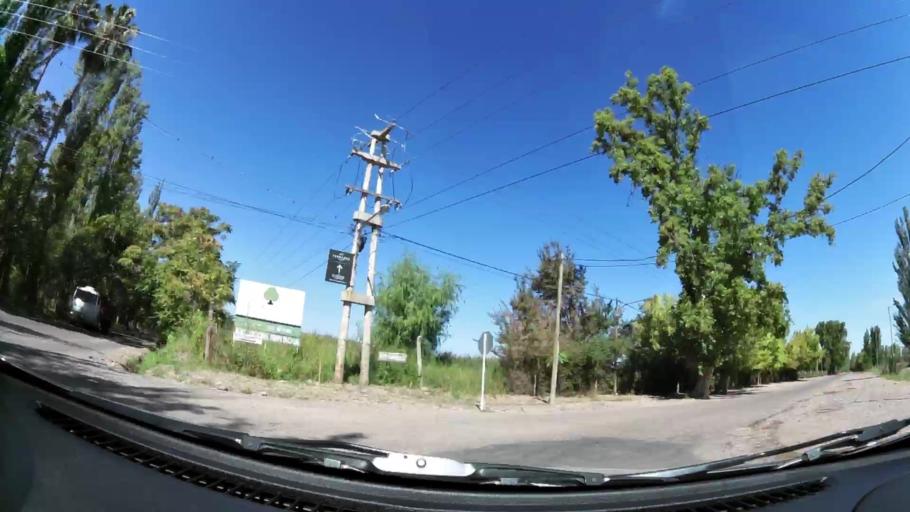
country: AR
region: Mendoza
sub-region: Departamento de Godoy Cruz
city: Godoy Cruz
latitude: -32.9860
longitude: -68.8438
